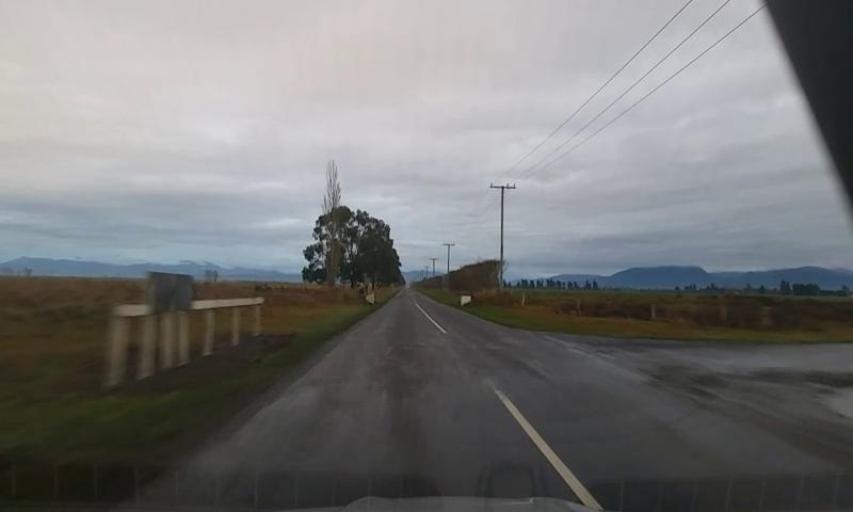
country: NZ
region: Canterbury
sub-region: Ashburton District
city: Methven
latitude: -43.7404
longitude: 171.6930
